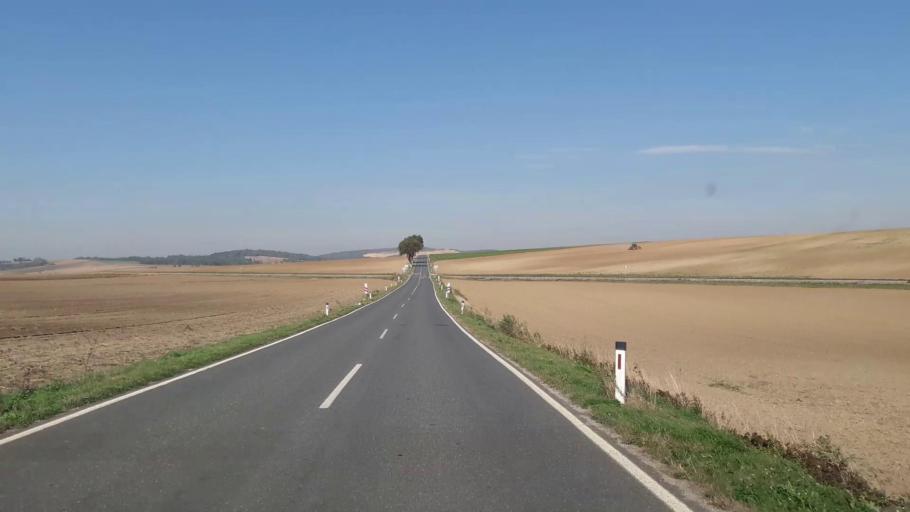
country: AT
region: Lower Austria
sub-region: Politischer Bezirk Korneuburg
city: Ernstbrunn
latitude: 48.5019
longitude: 16.3632
